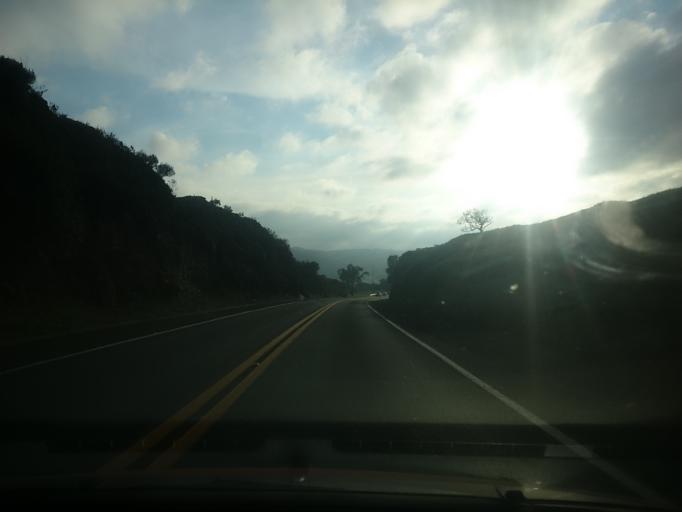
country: BR
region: Rio Grande do Sul
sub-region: Vacaria
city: Estrela
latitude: -28.1063
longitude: -50.6165
